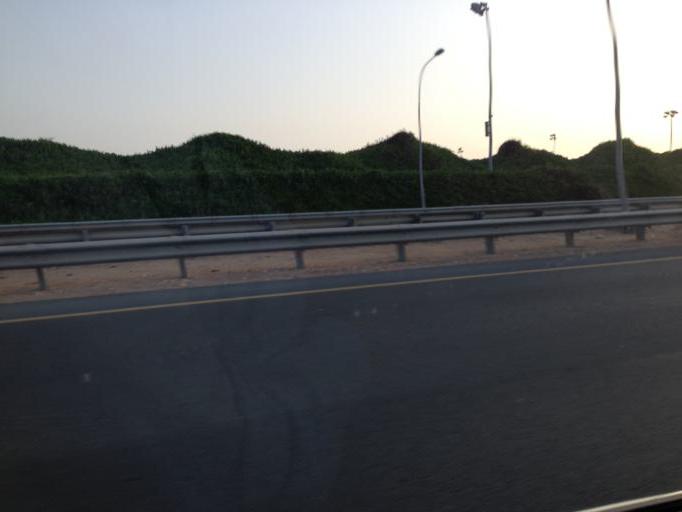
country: OM
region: Muhafazat Masqat
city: Bawshar
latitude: 23.6117
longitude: 58.3001
